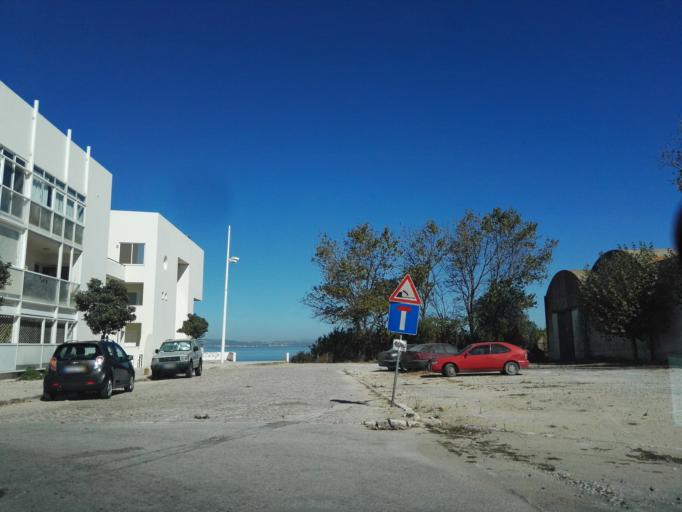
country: PT
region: Setubal
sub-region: Alcochete
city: Alcochete
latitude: 38.7573
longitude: -8.9581
